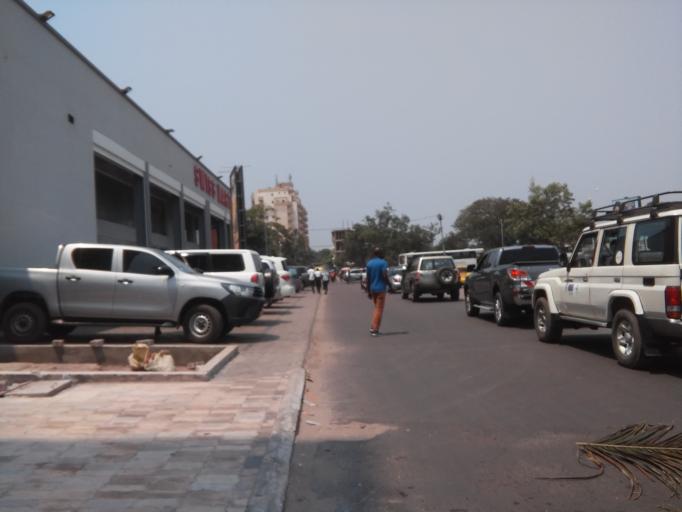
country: CD
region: Kinshasa
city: Kinshasa
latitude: -4.3169
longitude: 15.2915
